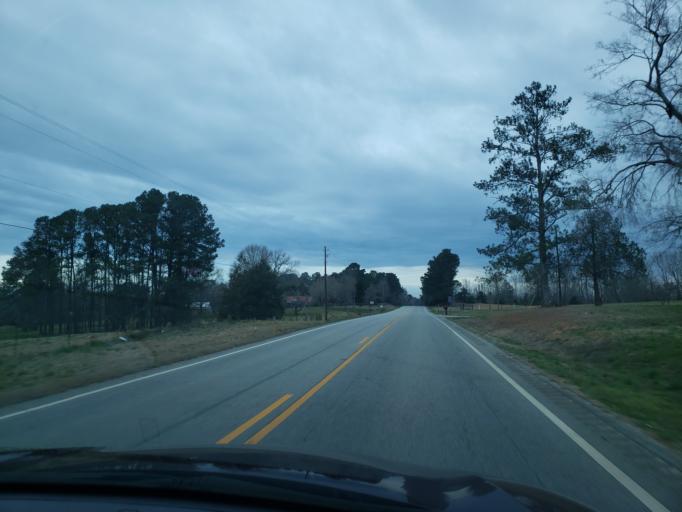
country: US
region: Alabama
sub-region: Chambers County
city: Lafayette
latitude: 32.9669
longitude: -85.4034
